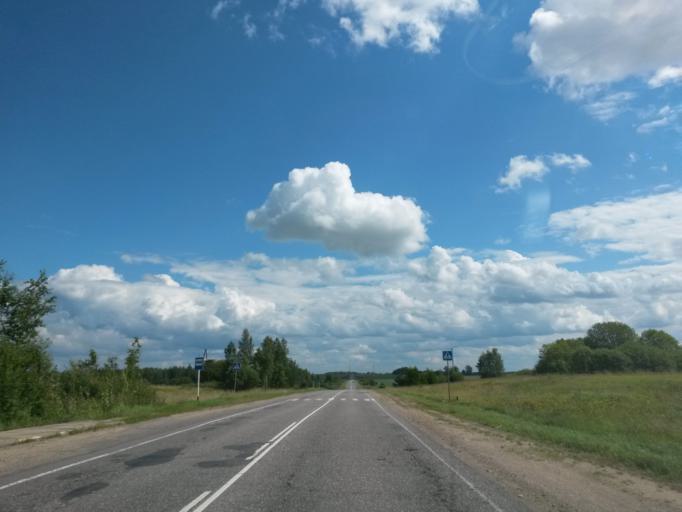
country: RU
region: Ivanovo
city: Pistsovo
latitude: 57.1857
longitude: 40.4598
